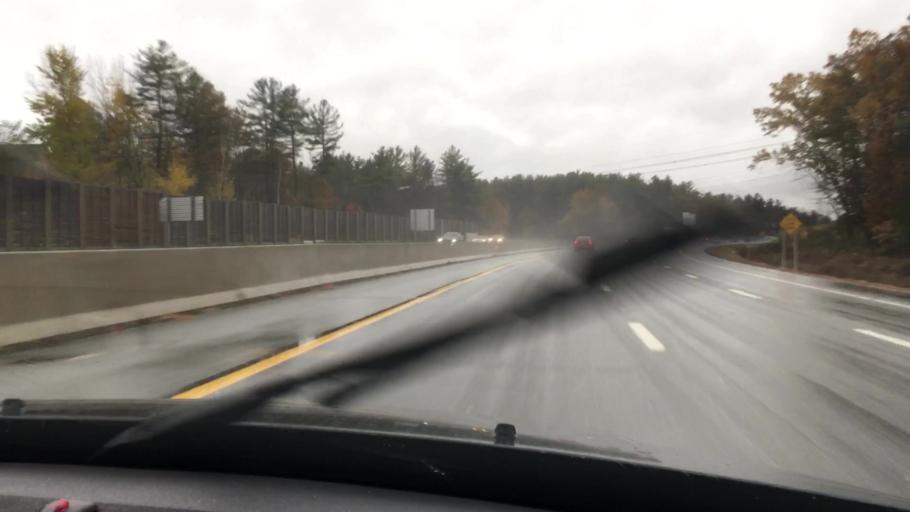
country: US
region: New Hampshire
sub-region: Hillsborough County
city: East Merrimack
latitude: 42.9030
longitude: -71.4638
